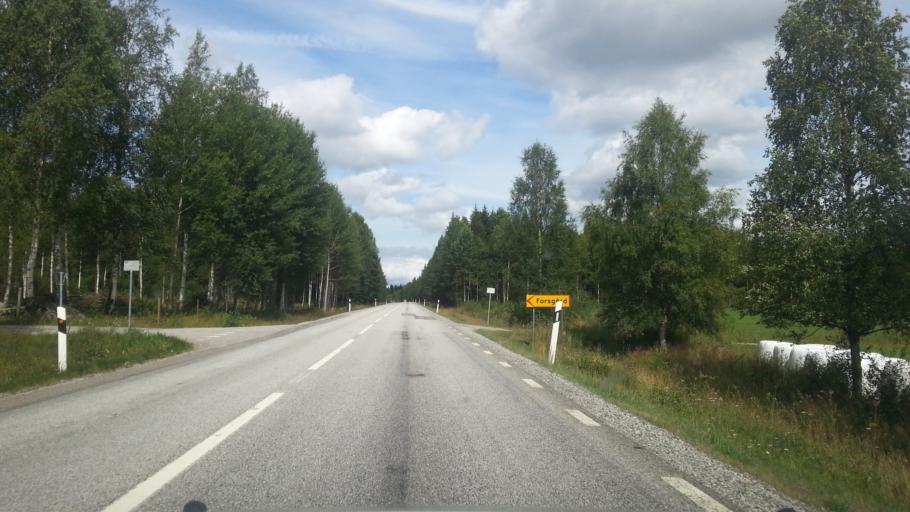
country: SE
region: Vaestmanland
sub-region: Skinnskattebergs Kommun
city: Skinnskatteberg
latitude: 59.7795
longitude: 15.5463
